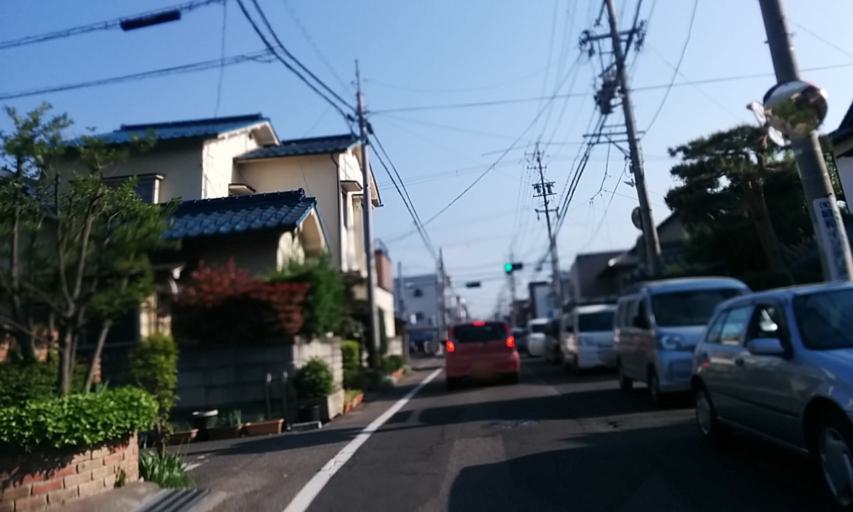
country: JP
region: Nagano
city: Matsumoto
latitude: 36.2374
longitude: 137.9816
